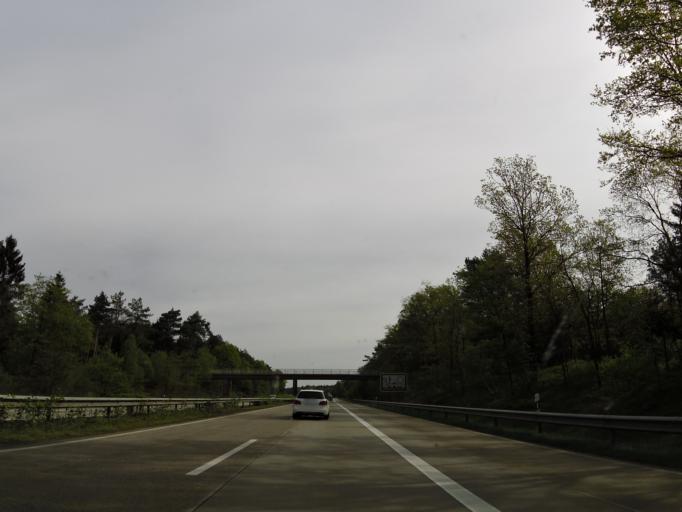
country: DE
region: Lower Saxony
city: Soltau
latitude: 52.9739
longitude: 9.9170
